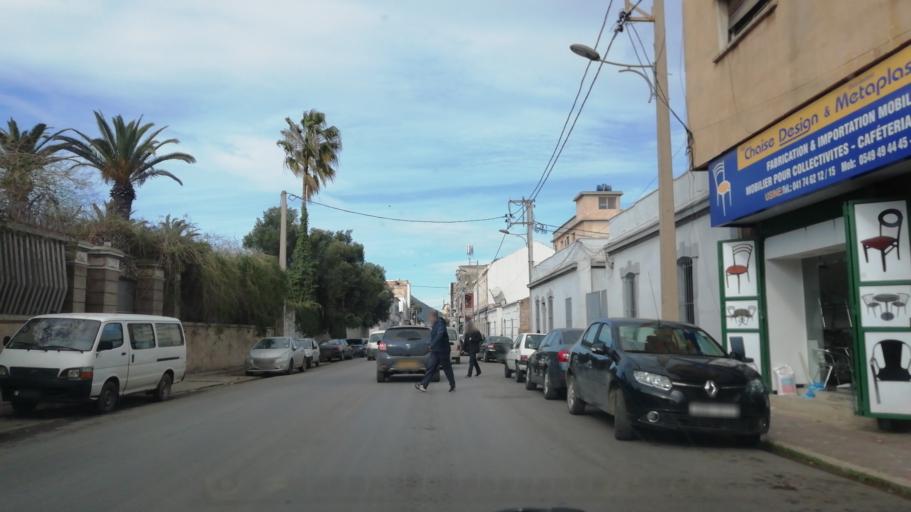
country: DZ
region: Oran
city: Oran
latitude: 35.6925
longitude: -0.6295
